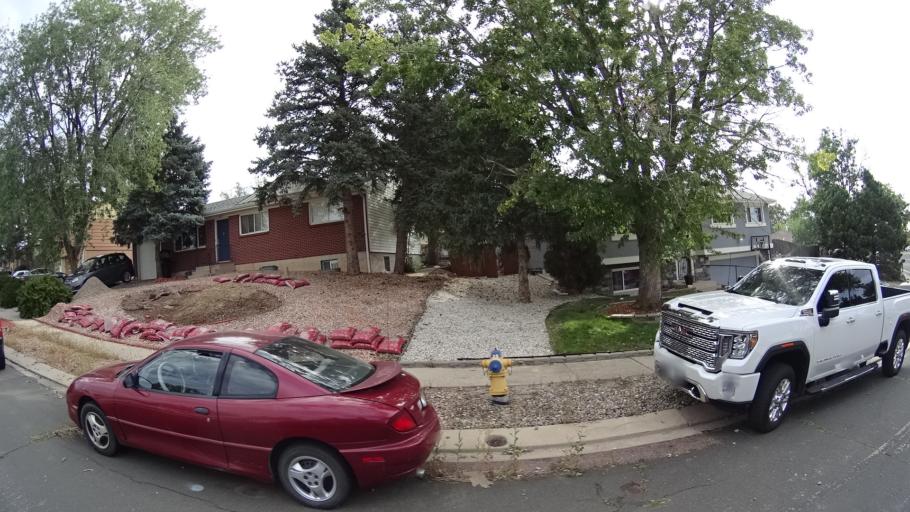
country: US
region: Colorado
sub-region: El Paso County
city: Cimarron Hills
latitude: 38.8415
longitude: -104.7519
